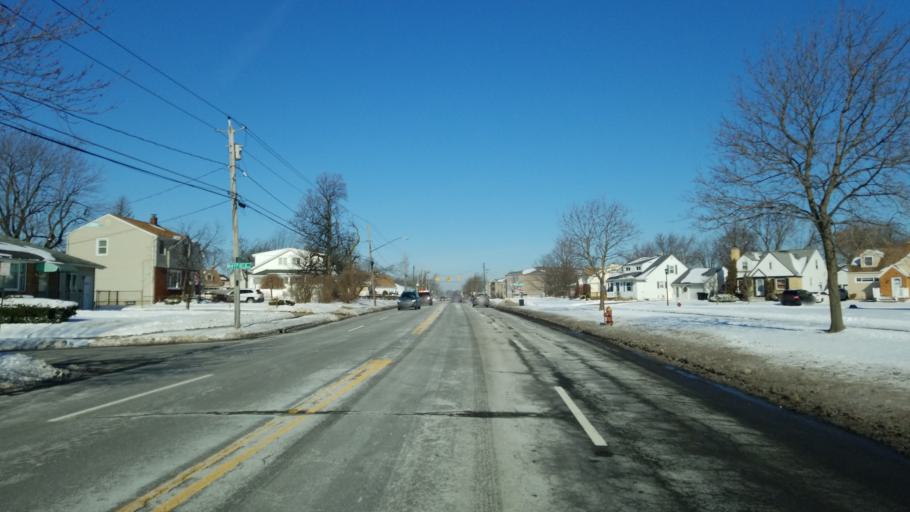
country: US
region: New York
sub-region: Erie County
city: Amherst
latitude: 42.9853
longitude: -78.8317
